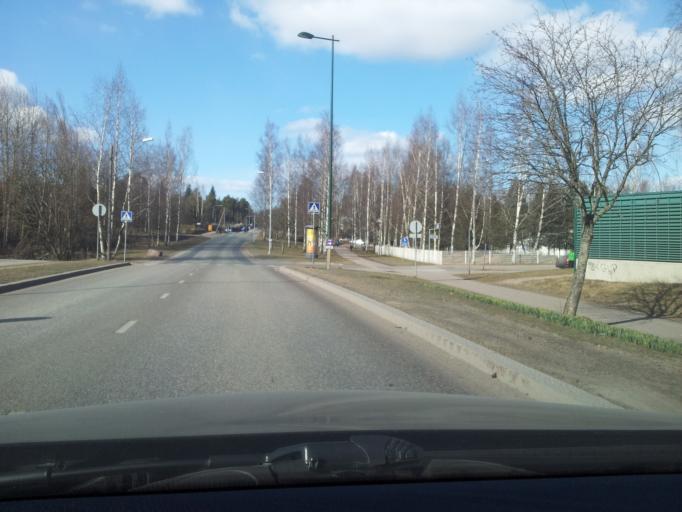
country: FI
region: Uusimaa
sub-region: Helsinki
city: Koukkuniemi
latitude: 60.1706
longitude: 24.7474
